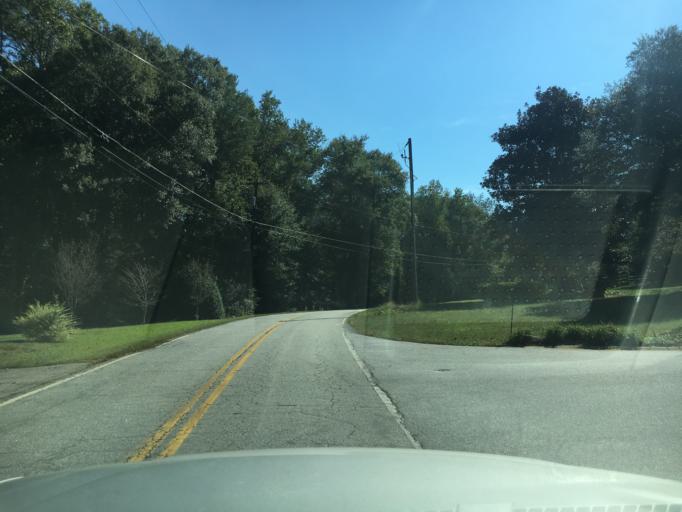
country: US
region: South Carolina
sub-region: Greenville County
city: Taylors
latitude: 34.9031
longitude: -82.2776
